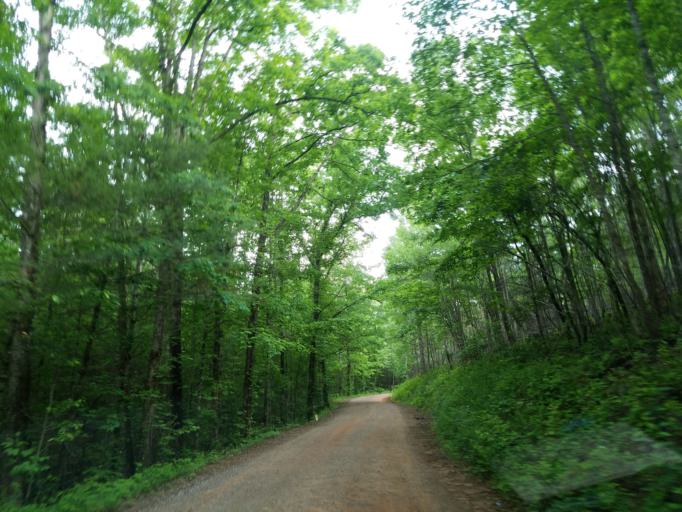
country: US
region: Georgia
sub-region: Lumpkin County
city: Dahlonega
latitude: 34.5918
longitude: -84.1187
